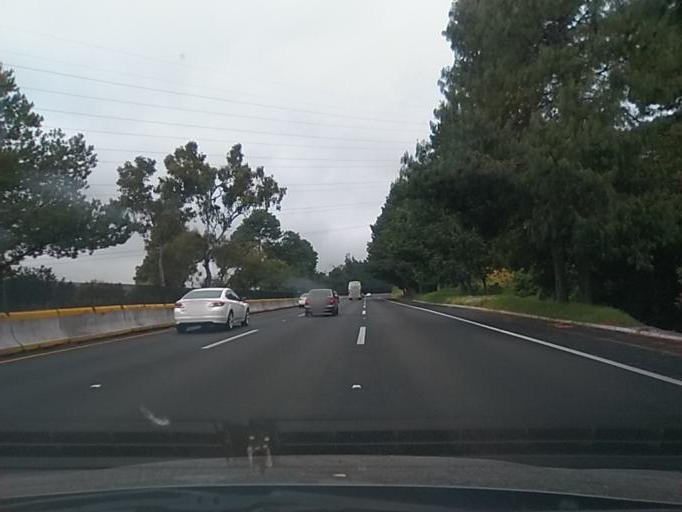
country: MX
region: Mexico City
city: Xochimilco
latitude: 19.1853
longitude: -99.1566
